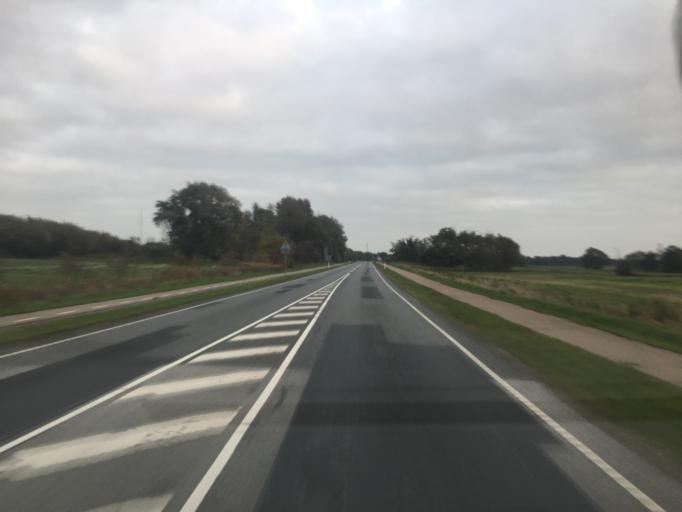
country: DK
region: South Denmark
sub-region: Tonder Kommune
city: Tonder
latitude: 54.9478
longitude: 8.8355
